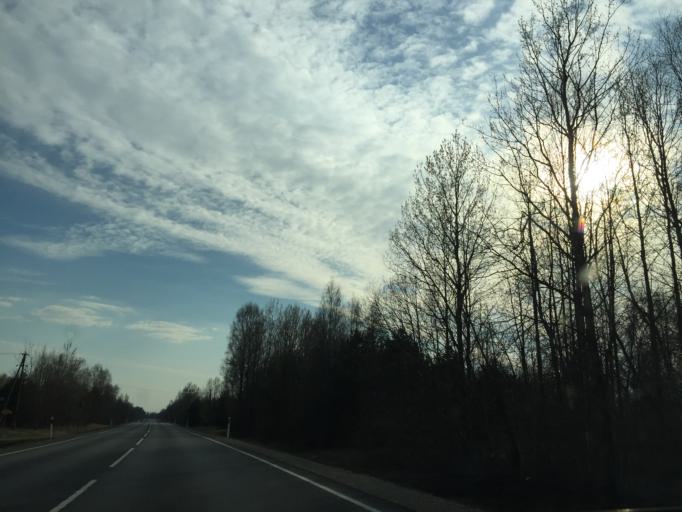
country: EE
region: Jogevamaa
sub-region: Mustvee linn
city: Mustvee
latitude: 58.9516
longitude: 27.0612
